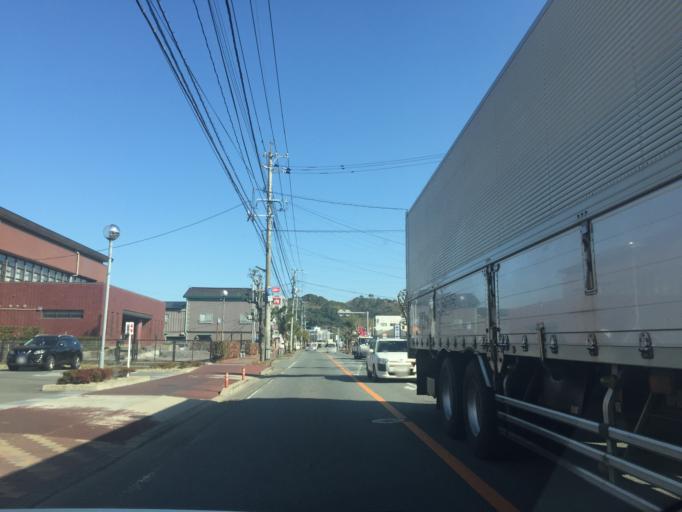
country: JP
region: Fukuoka
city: Umi
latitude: 33.5891
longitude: 130.4815
